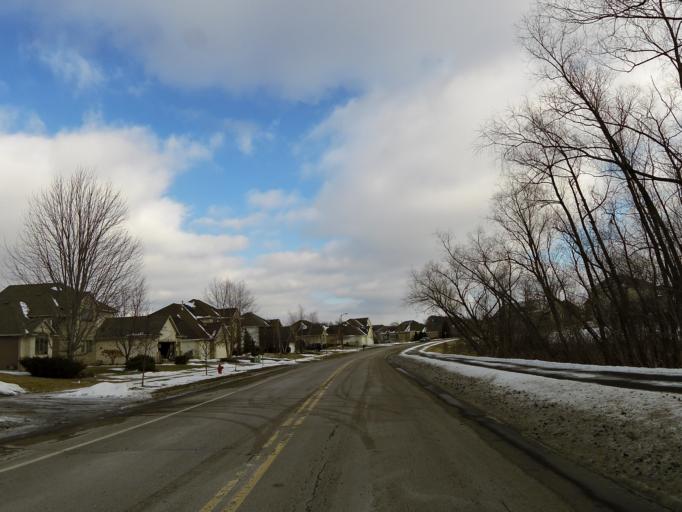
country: US
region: Minnesota
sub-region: Scott County
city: Prior Lake
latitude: 44.7285
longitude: -93.4536
